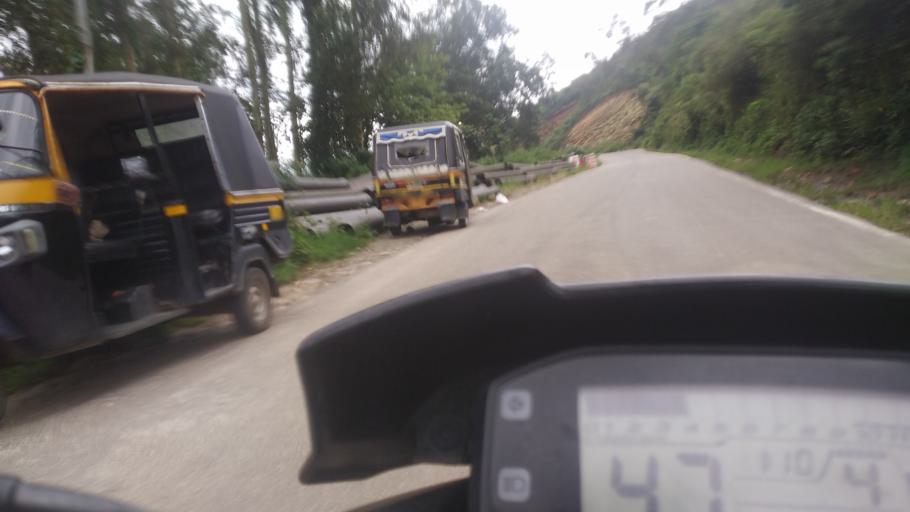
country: IN
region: Kerala
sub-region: Idukki
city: Munnar
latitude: 10.0842
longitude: 77.0655
